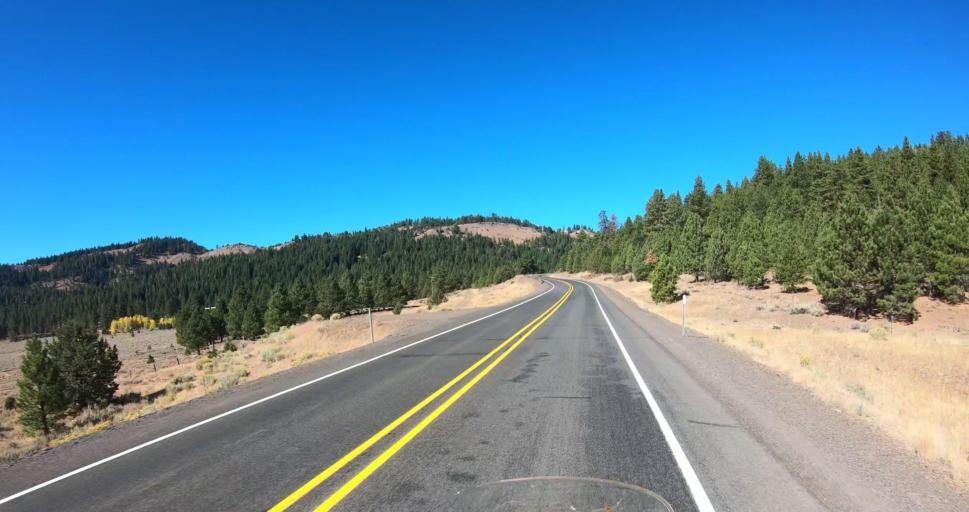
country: US
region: Oregon
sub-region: Lake County
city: Lakeview
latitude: 42.2291
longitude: -120.2815
